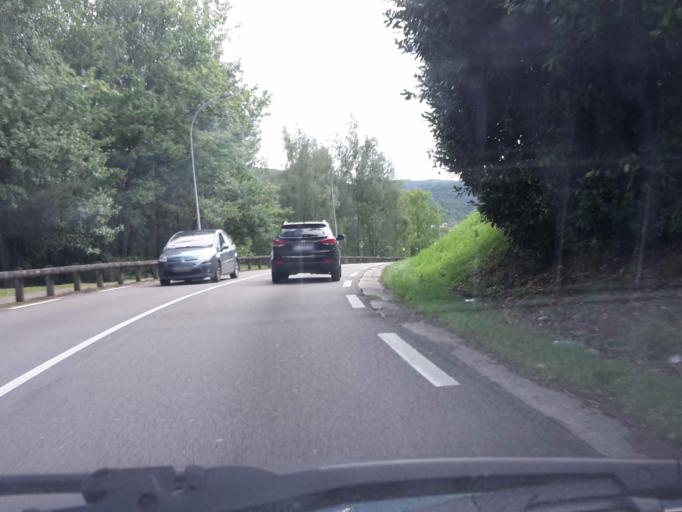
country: FR
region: Franche-Comte
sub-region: Departement du Doubs
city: Avanne-Aveney
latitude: 47.2178
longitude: 5.9586
